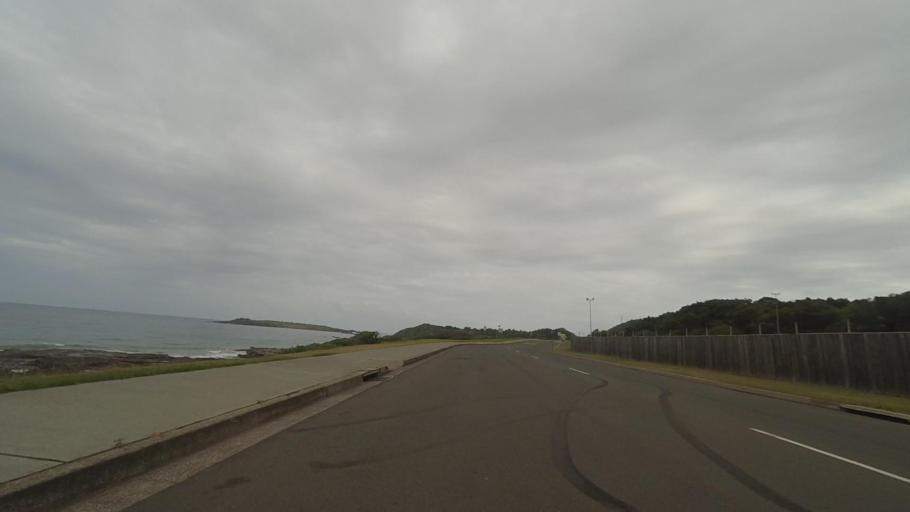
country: AU
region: New South Wales
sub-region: Wollongong
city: Port Kembla
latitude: -34.4834
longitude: 150.9140
